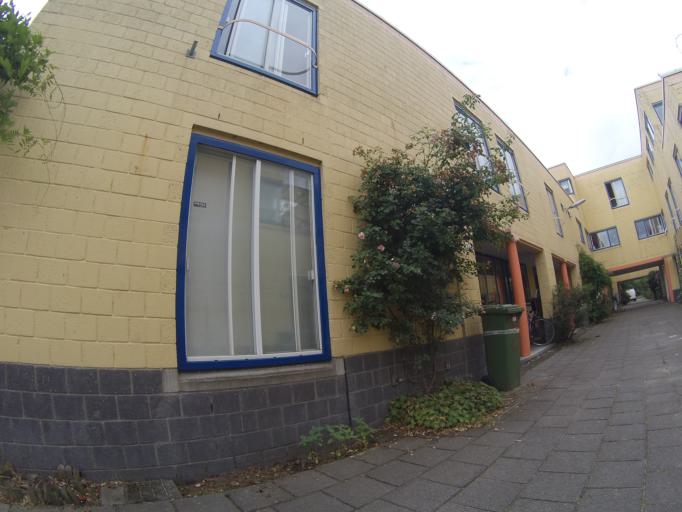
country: NL
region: Utrecht
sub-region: Gemeente Amersfoort
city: Amersfoort
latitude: 52.1754
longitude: 5.3973
